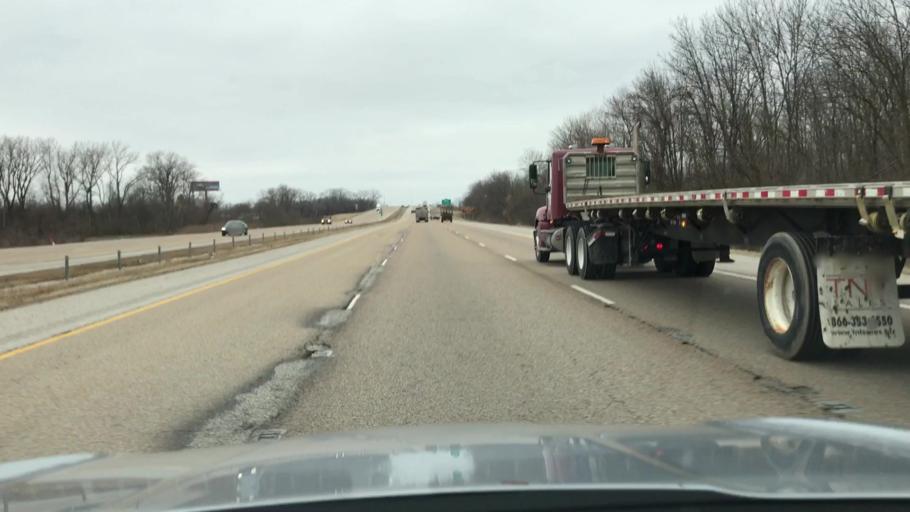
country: US
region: Illinois
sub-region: Saint Clair County
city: Fairmont City
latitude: 38.6628
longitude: -90.0712
